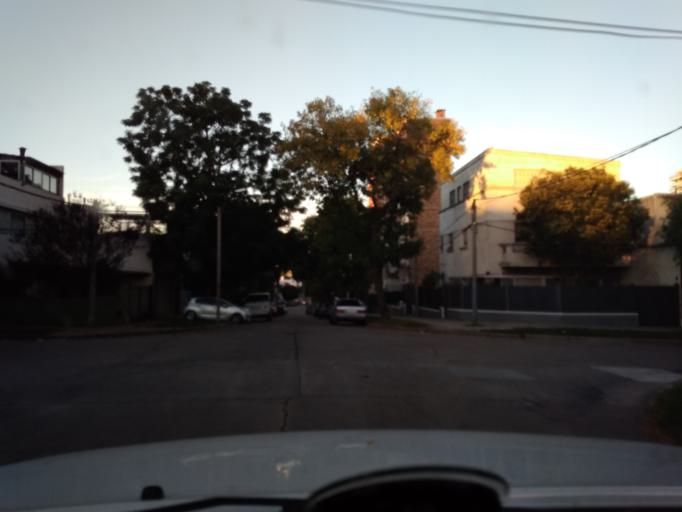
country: UY
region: Montevideo
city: Montevideo
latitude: -34.8950
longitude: -56.1241
